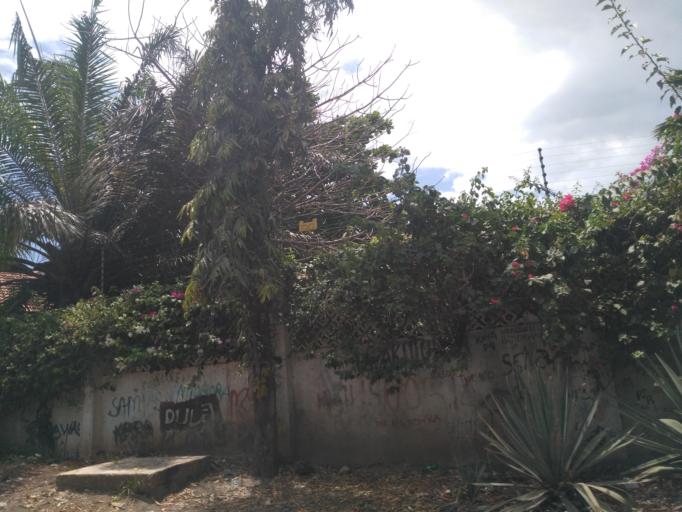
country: TZ
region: Dar es Salaam
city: Magomeni
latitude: -6.7706
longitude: 39.2716
